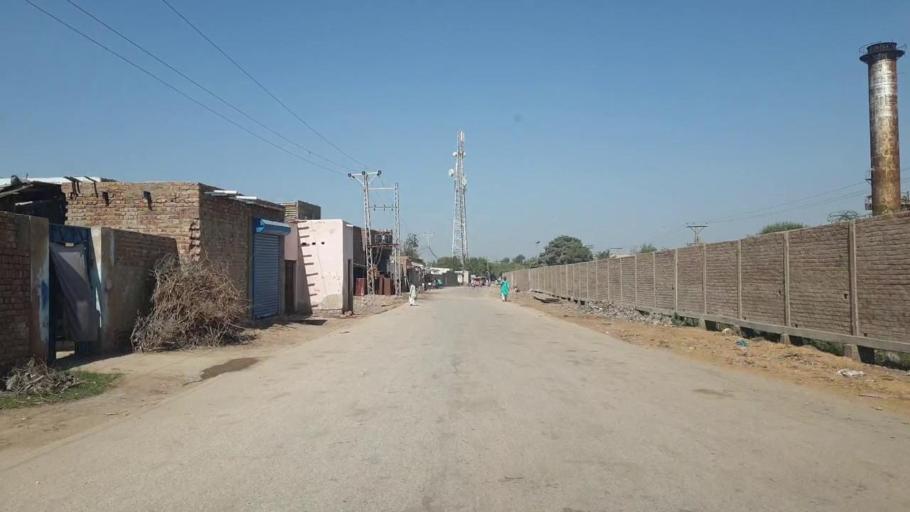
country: PK
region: Sindh
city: Talhar
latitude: 24.8817
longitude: 68.8193
